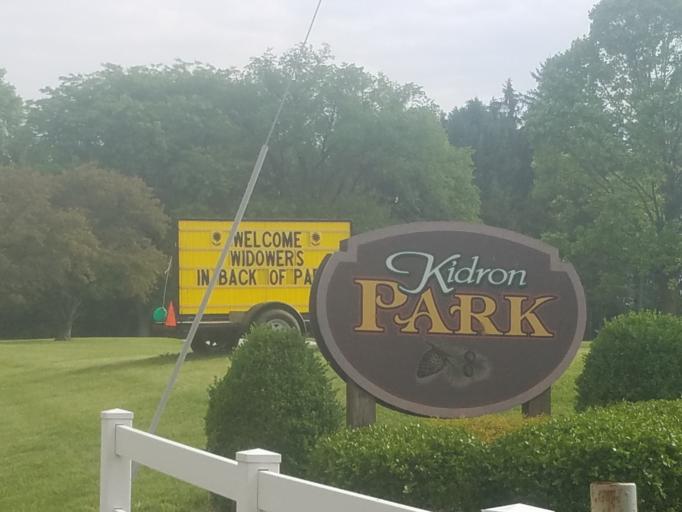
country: US
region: Ohio
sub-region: Wayne County
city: Dalton
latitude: 40.7446
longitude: -81.7450
